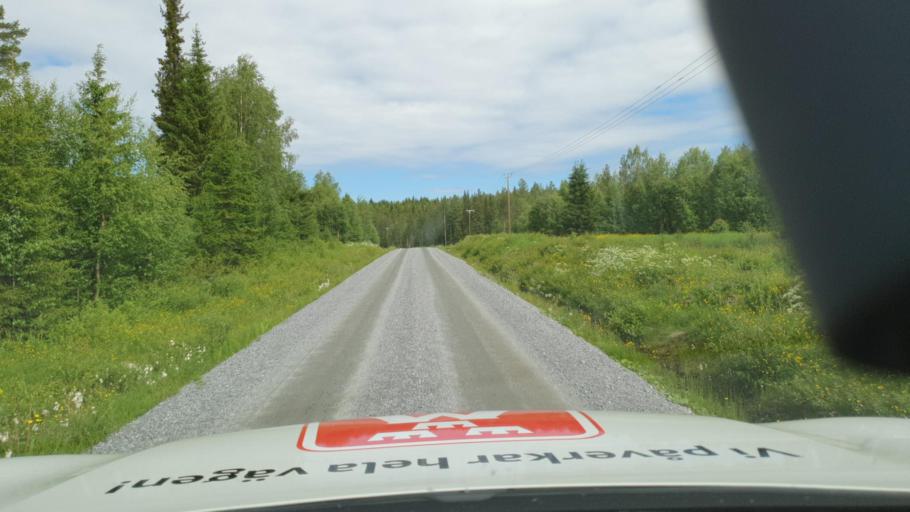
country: SE
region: Vaesterbotten
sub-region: Skelleftea Kommun
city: Langsele
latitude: 64.6098
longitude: 20.2716
